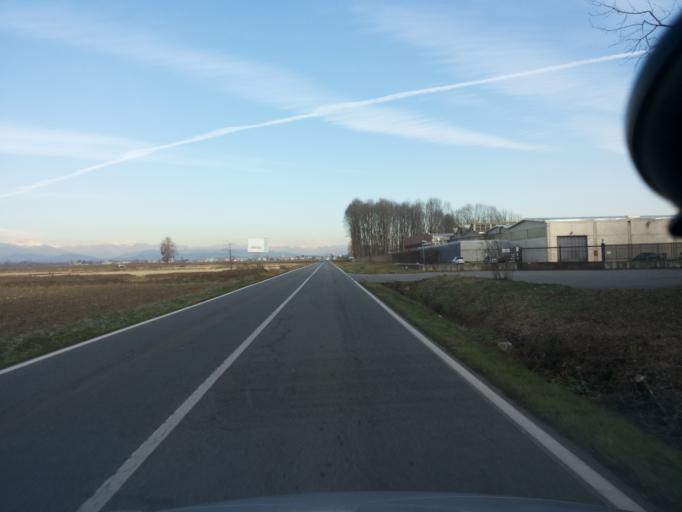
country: IT
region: Piedmont
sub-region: Provincia di Vercelli
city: Greggio
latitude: 45.4707
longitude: 8.3869
